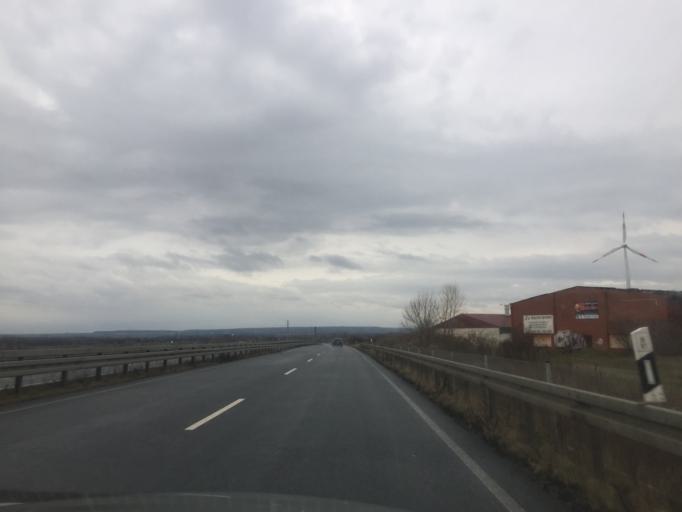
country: DE
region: Saxony-Anhalt
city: Wolmirsleben
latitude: 51.9695
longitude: 11.4582
